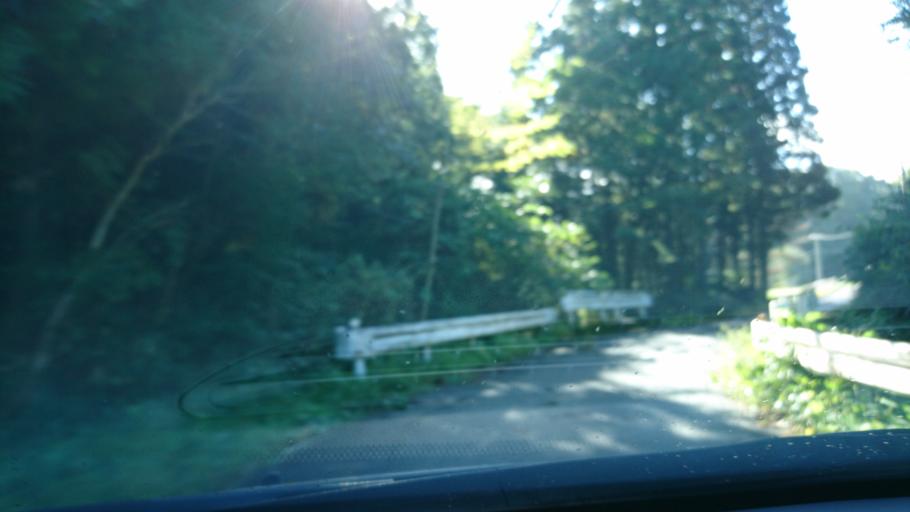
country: JP
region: Iwate
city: Ichinoseki
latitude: 38.9537
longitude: 141.0019
